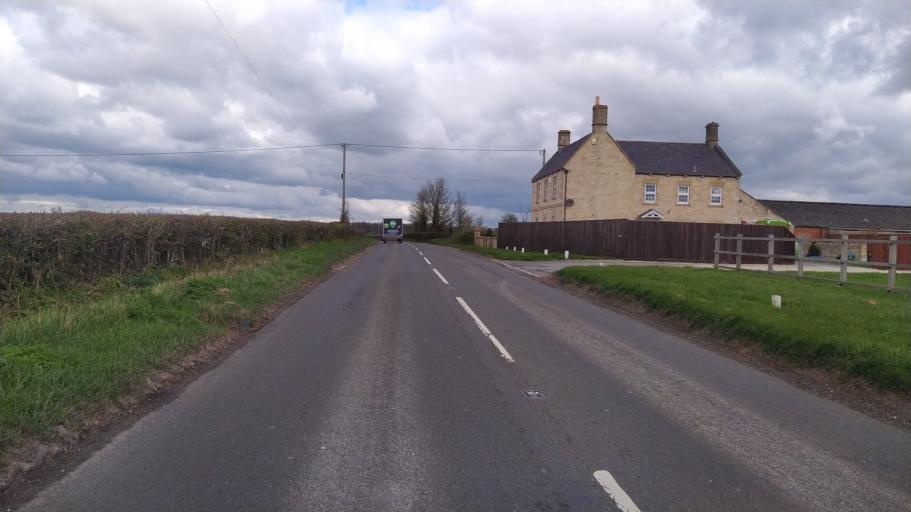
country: GB
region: England
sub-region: Wiltshire
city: North Bradley
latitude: 51.3092
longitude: -2.1859
